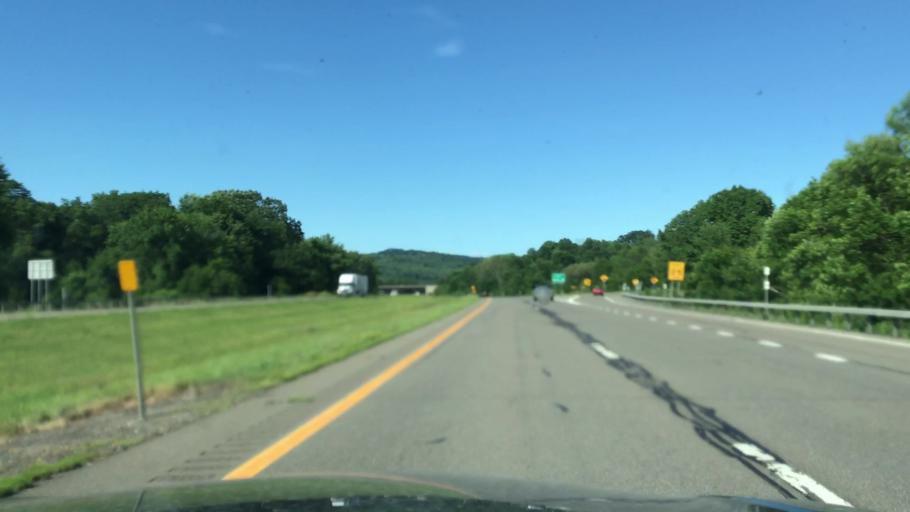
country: US
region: New York
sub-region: Tioga County
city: Owego
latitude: 42.0936
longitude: -76.2665
